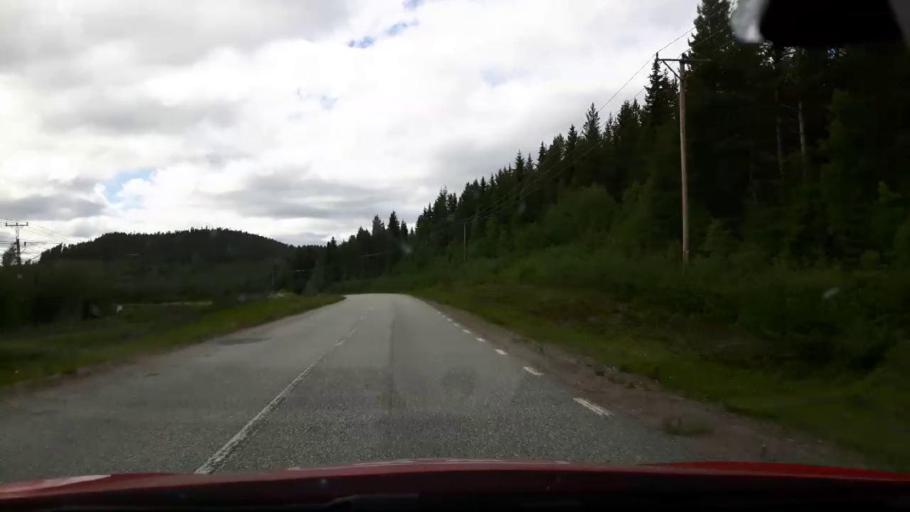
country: SE
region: Jaemtland
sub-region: Ragunda Kommun
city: Hammarstrand
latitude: 62.9663
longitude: 16.0158
